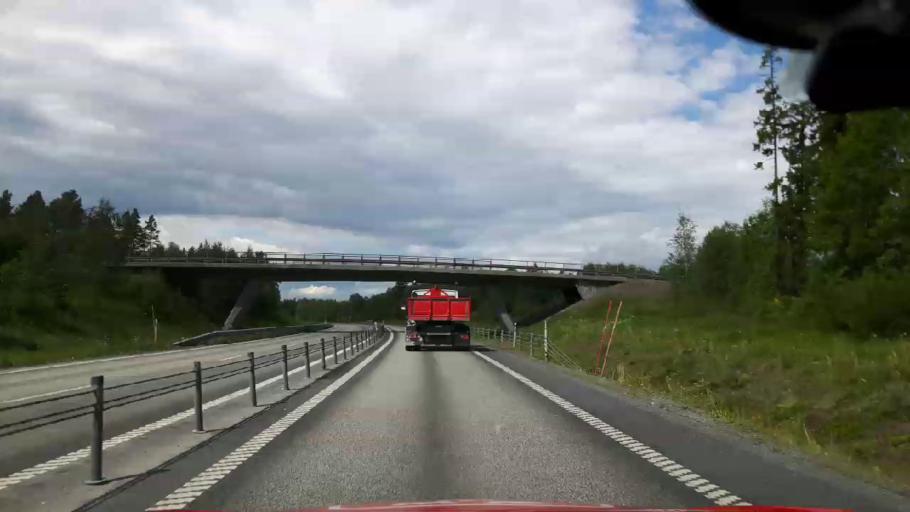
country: SE
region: Jaemtland
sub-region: OEstersunds Kommun
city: Ostersund
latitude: 63.2114
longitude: 14.6613
